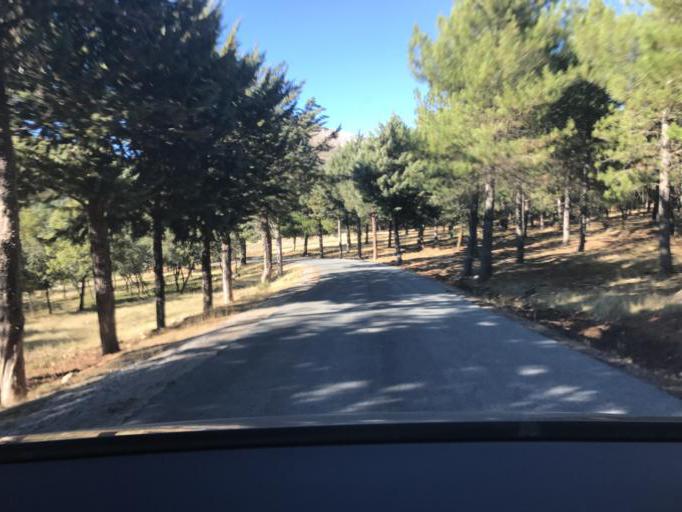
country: ES
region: Andalusia
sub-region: Provincia de Granada
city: Beas de Granada
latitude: 37.3048
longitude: -3.4523
